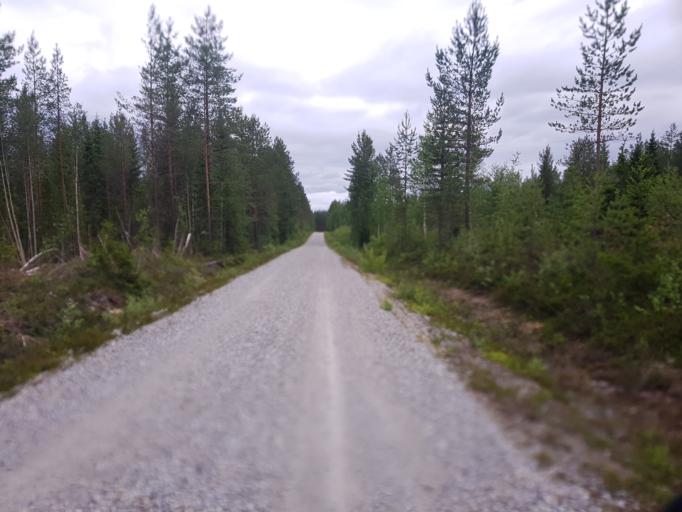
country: FI
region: Kainuu
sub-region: Kehys-Kainuu
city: Kuhmo
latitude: 64.4540
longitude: 29.7106
